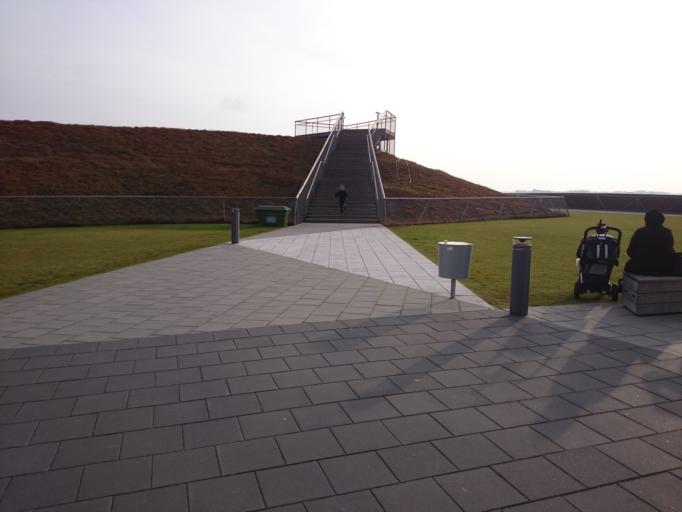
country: SE
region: Skane
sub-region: Malmo
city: Bunkeflostrand
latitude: 55.5643
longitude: 12.9725
